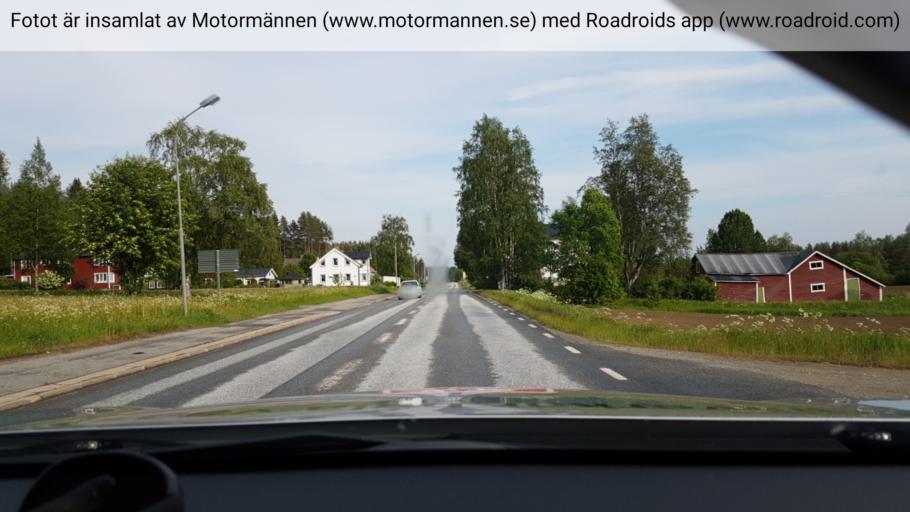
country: SE
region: Vaesterbotten
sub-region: Bjurholms Kommun
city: Bjurholm
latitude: 64.2451
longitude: 19.3225
